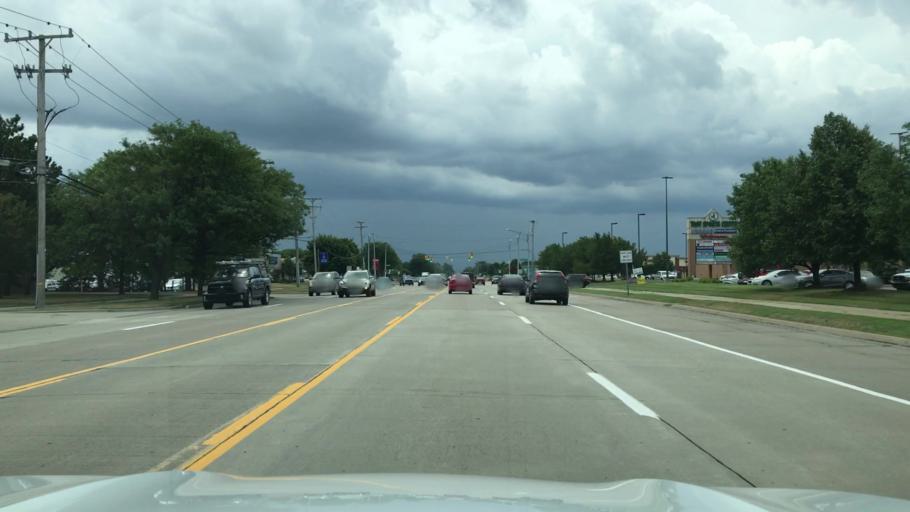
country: US
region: Michigan
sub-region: Oakland County
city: Clawson
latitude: 42.5656
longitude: -83.1084
